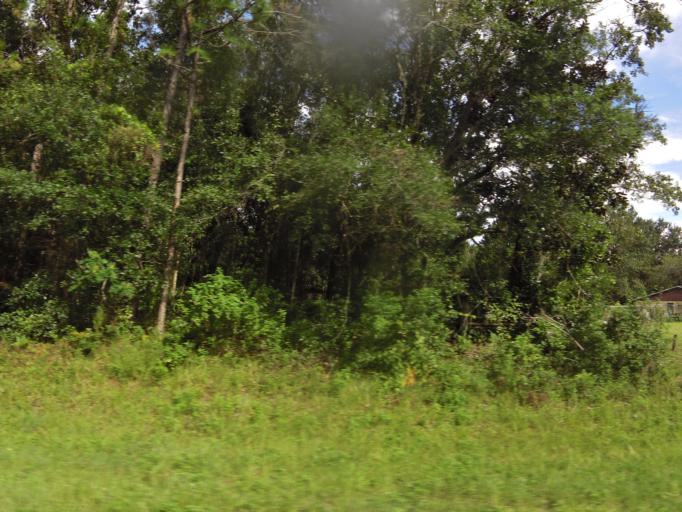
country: US
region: Florida
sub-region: Clay County
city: Green Cove Springs
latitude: 29.9240
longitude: -81.6808
